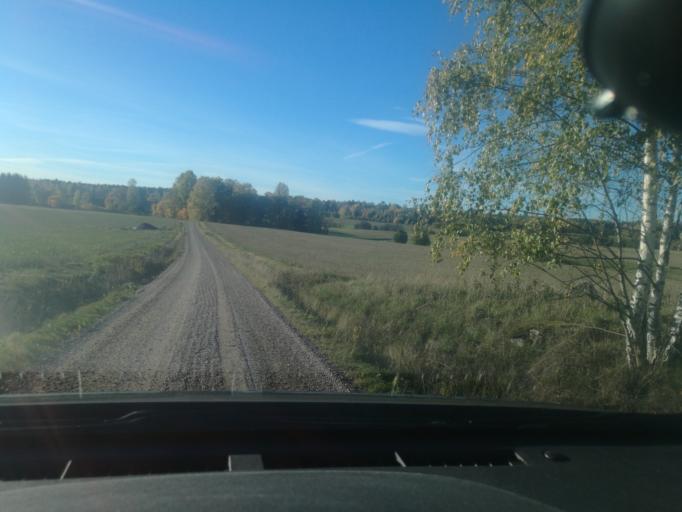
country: SE
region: Vaestmanland
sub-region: Kopings Kommun
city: Koping
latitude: 59.5949
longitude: 16.0114
